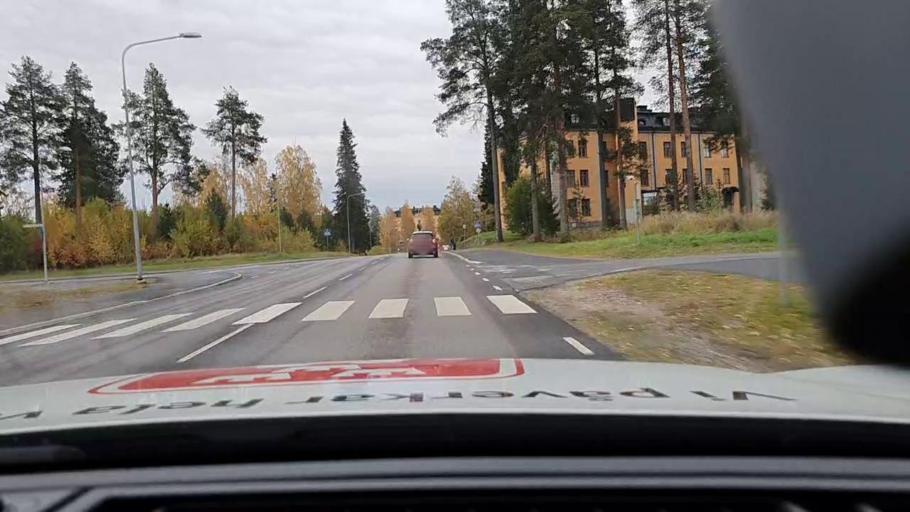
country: SE
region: Norrbotten
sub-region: Bodens Kommun
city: Boden
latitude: 65.8152
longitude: 21.6741
